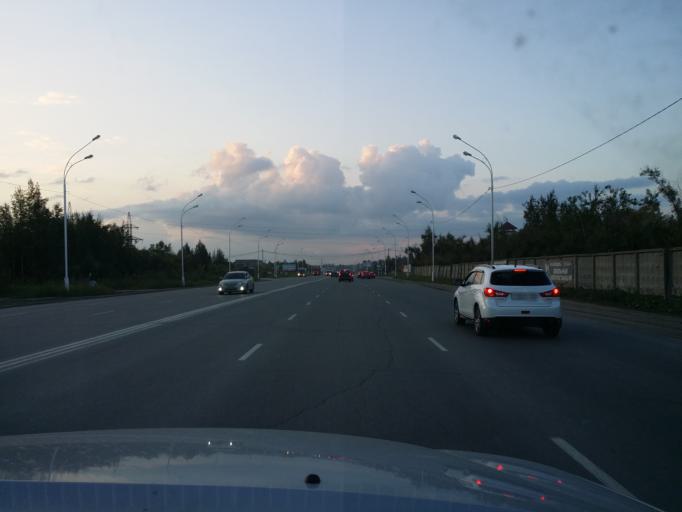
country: RU
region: Khanty-Mansiyskiy Avtonomnyy Okrug
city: Nizhnevartovsk
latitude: 60.9574
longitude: 76.5303
